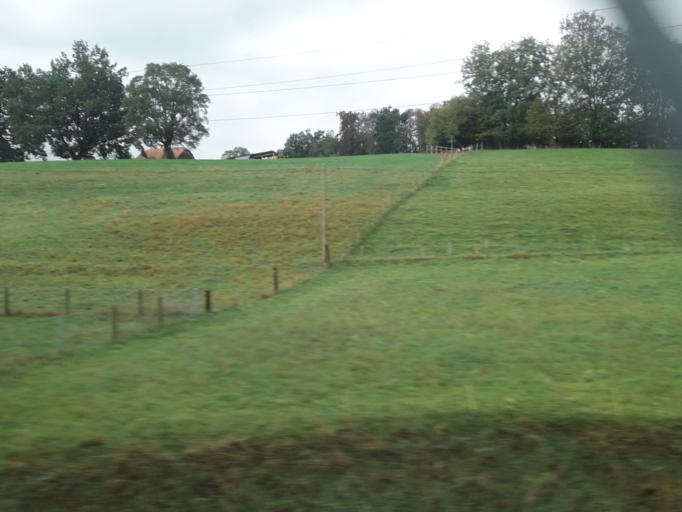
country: CH
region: Bern
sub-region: Thun District
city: Uetendorf
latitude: 46.7858
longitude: 7.5621
